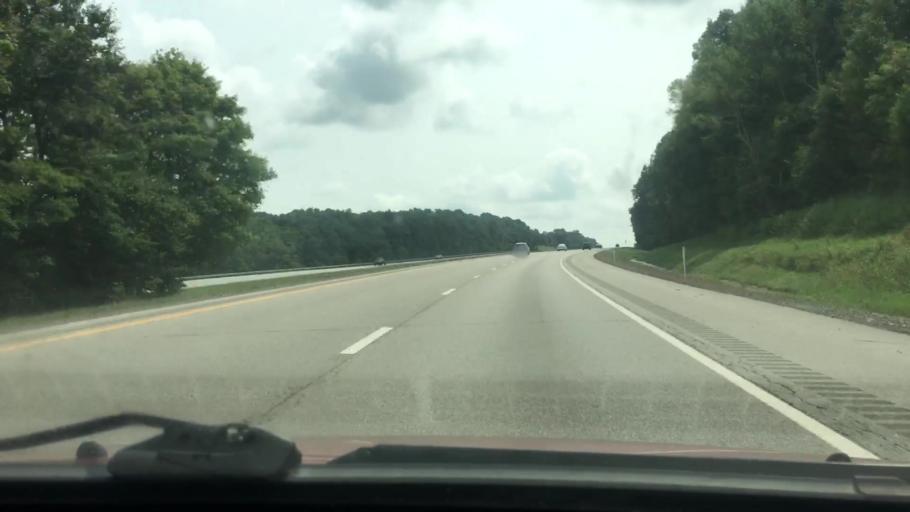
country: US
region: West Virginia
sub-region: Preston County
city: Kingwood
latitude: 39.6628
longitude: -79.5897
